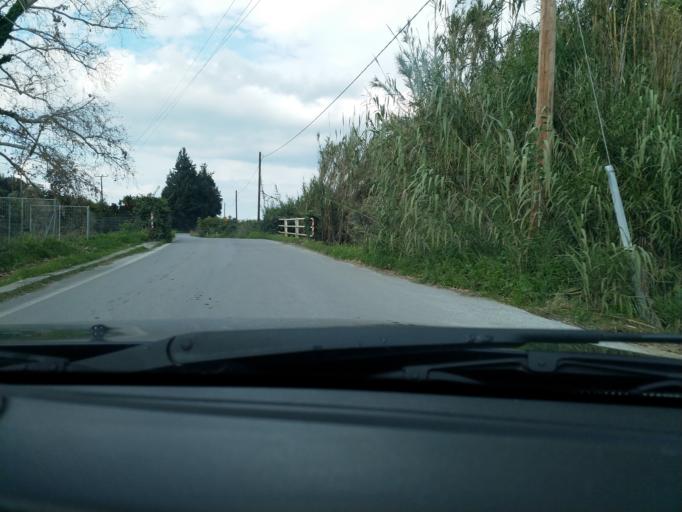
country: GR
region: Crete
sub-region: Nomos Chanias
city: Gerani
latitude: 35.5050
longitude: 23.8961
